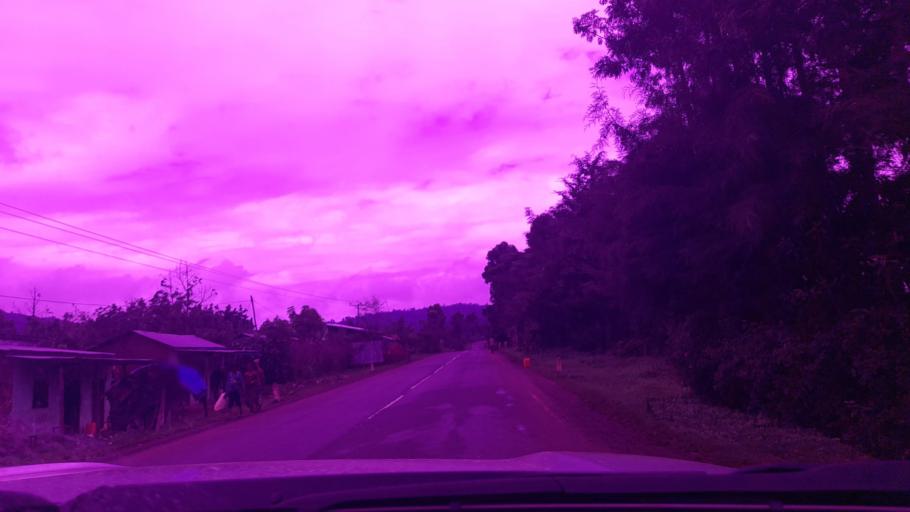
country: ET
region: Oromiya
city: Jima
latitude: 7.5548
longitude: 36.6140
